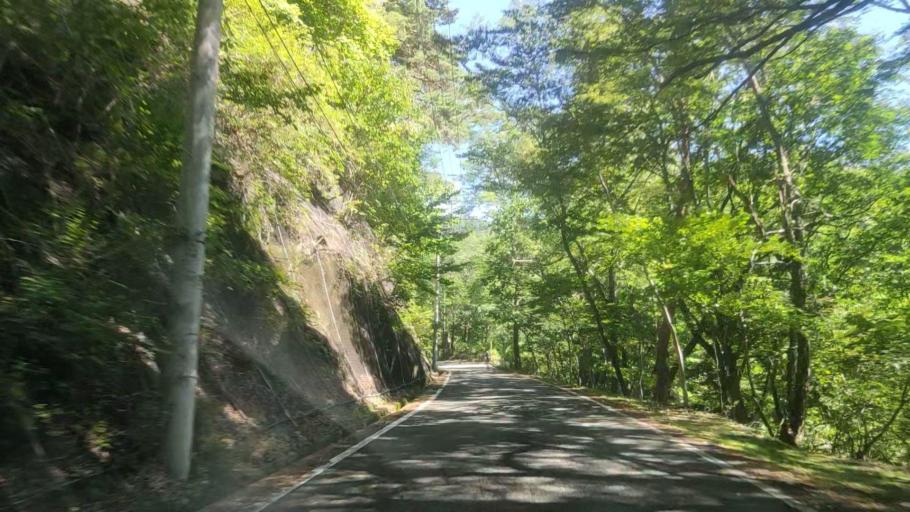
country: JP
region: Yamanashi
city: Fujikawaguchiko
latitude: 35.5502
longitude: 138.7774
